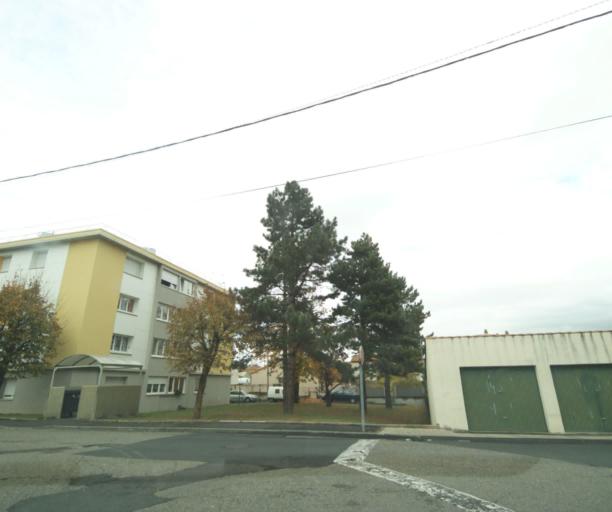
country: FR
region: Auvergne
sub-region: Departement du Puy-de-Dome
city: Pont-du-Chateau
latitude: 45.8003
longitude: 3.2468
